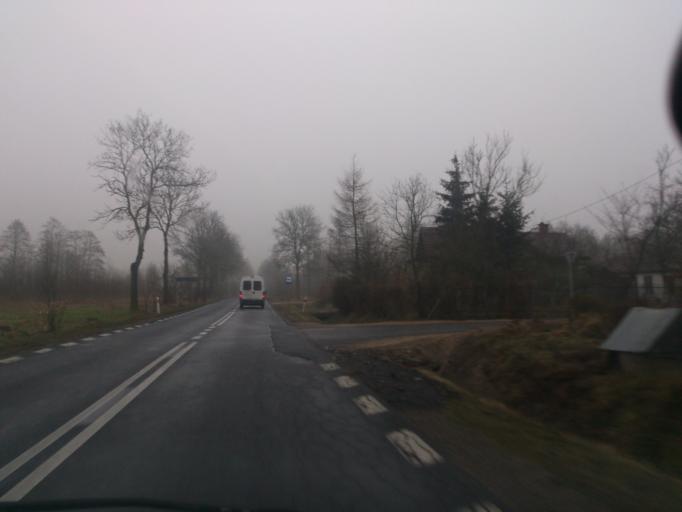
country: PL
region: Masovian Voivodeship
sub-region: Powiat sierpecki
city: Szczutowo
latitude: 52.9125
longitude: 19.6297
